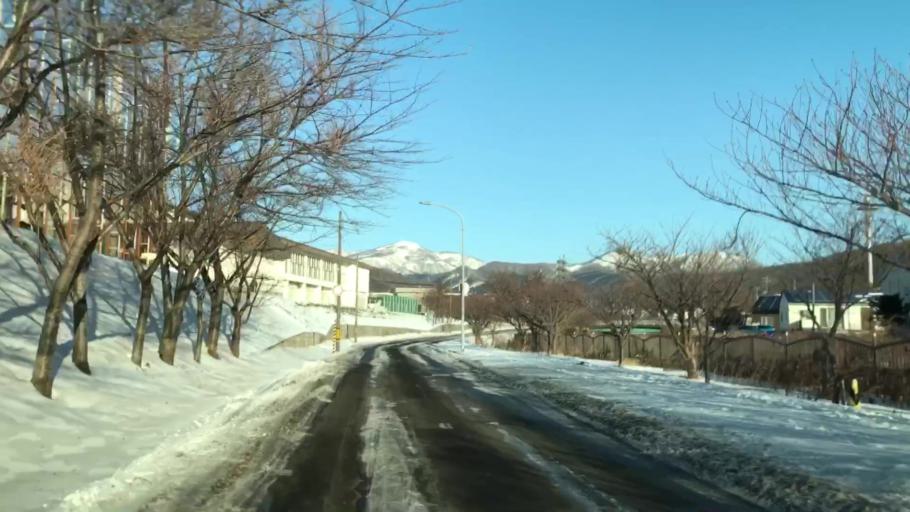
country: JP
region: Hokkaido
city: Muroran
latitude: 42.3687
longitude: 141.0381
